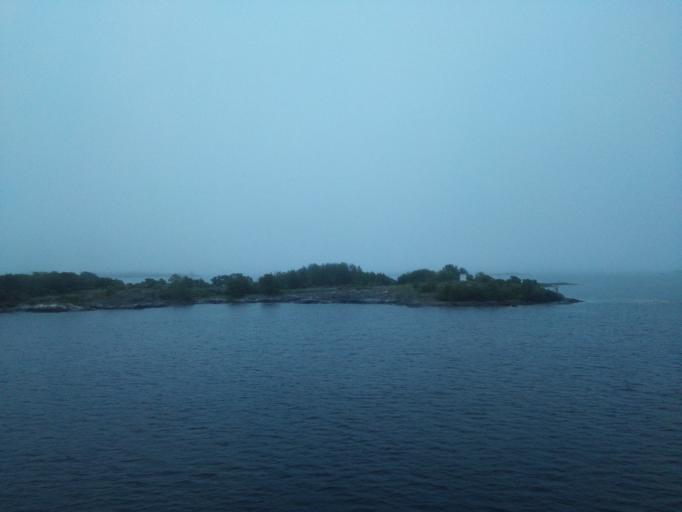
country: SE
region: Stockholm
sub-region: Norrtalje Kommun
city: Bjorko
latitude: 59.7383
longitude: 19.2305
